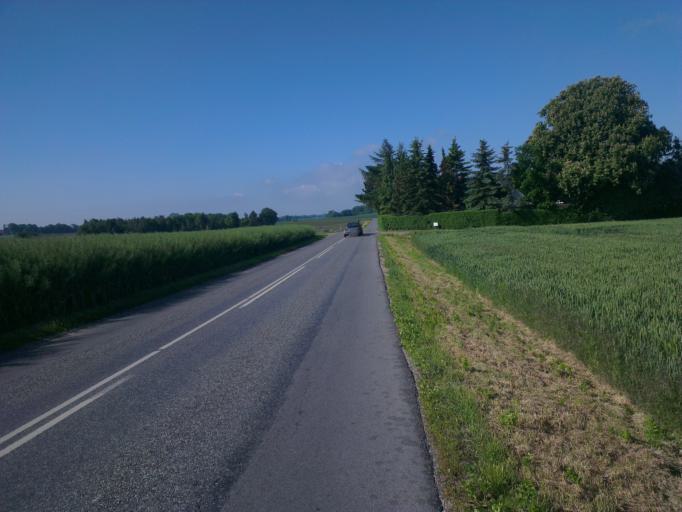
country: DK
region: Capital Region
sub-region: Frederikssund Kommune
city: Frederikssund
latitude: 55.7959
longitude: 12.0155
